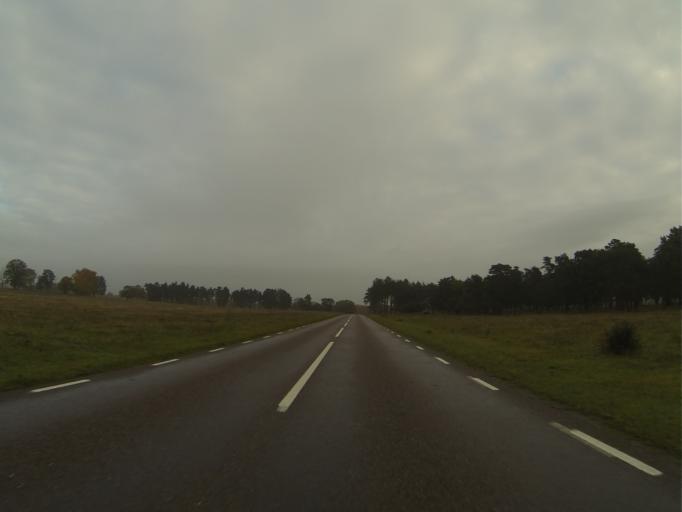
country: SE
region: Skane
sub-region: Lunds Kommun
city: Veberod
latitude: 55.6661
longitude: 13.4893
